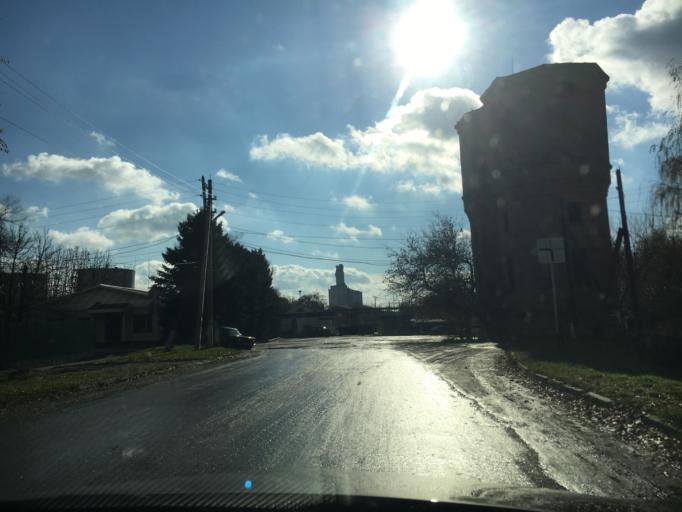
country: RU
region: Rostov
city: Matveyev Kurgan
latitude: 47.5628
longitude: 38.8620
